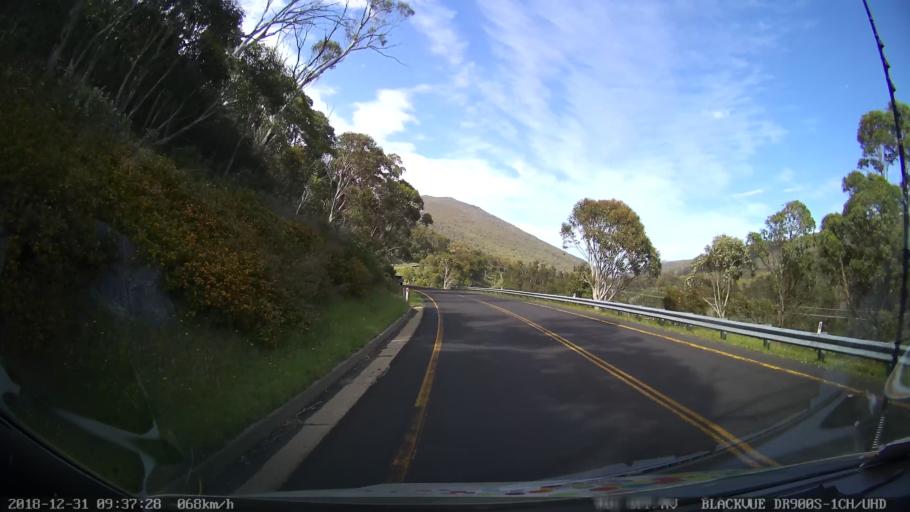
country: AU
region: New South Wales
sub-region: Snowy River
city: Jindabyne
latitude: -36.4666
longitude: 148.3753
